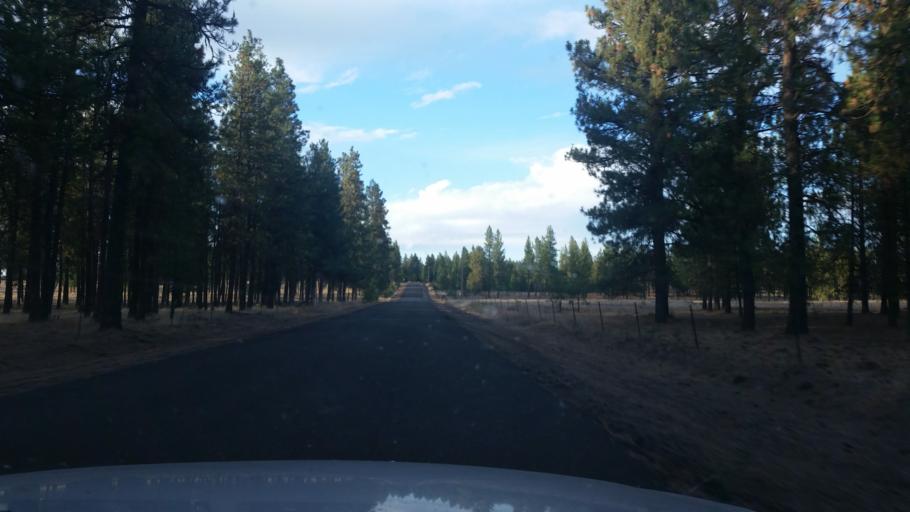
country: US
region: Washington
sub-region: Spokane County
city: Medical Lake
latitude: 47.4455
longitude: -117.7898
